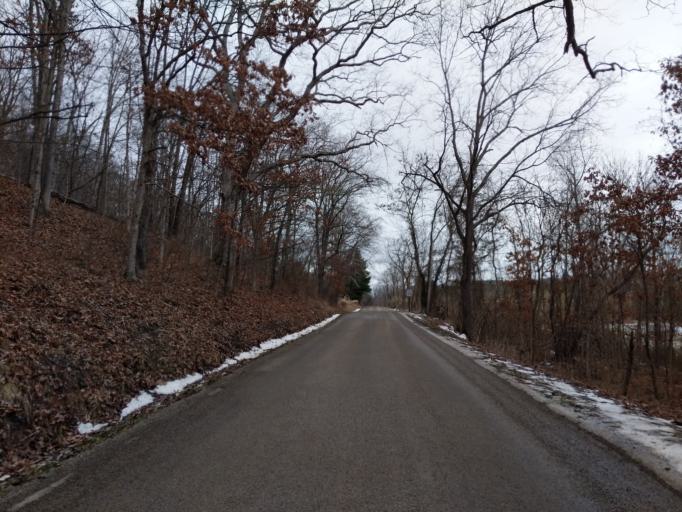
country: US
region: Ohio
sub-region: Athens County
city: The Plains
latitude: 39.3337
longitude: -82.1425
